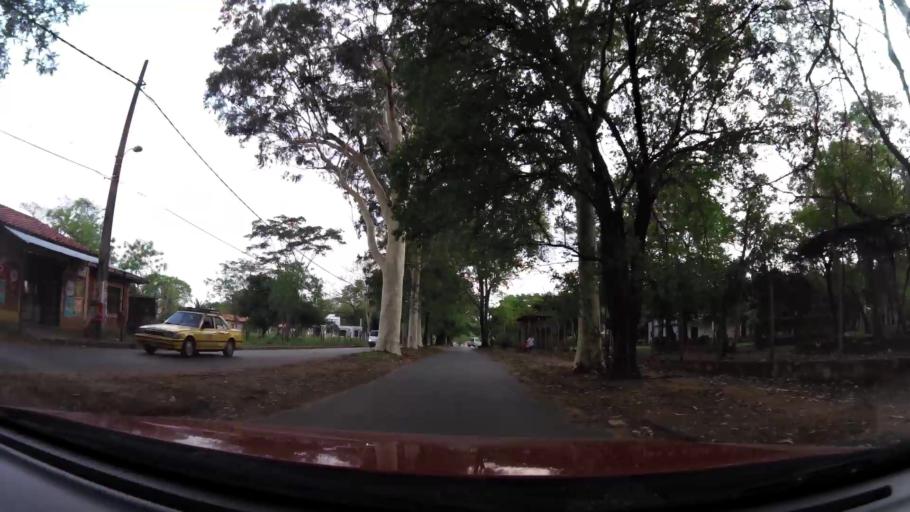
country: PY
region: Central
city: Fernando de la Mora
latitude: -25.3613
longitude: -57.5227
